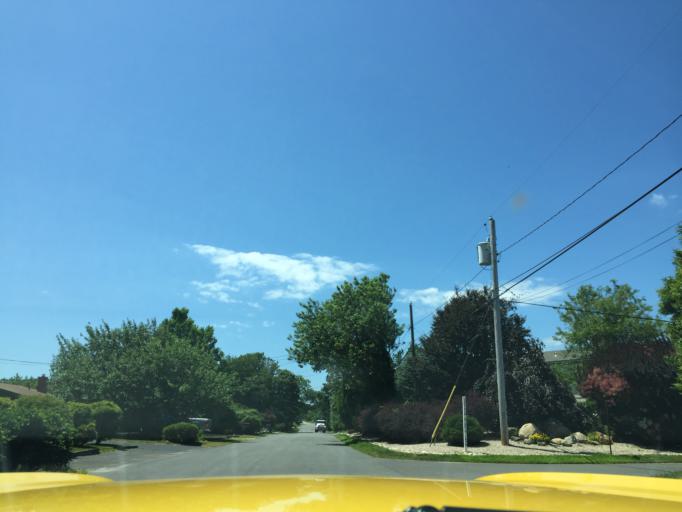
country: US
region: New York
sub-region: Suffolk County
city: Montauk
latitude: 41.0717
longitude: -71.9522
